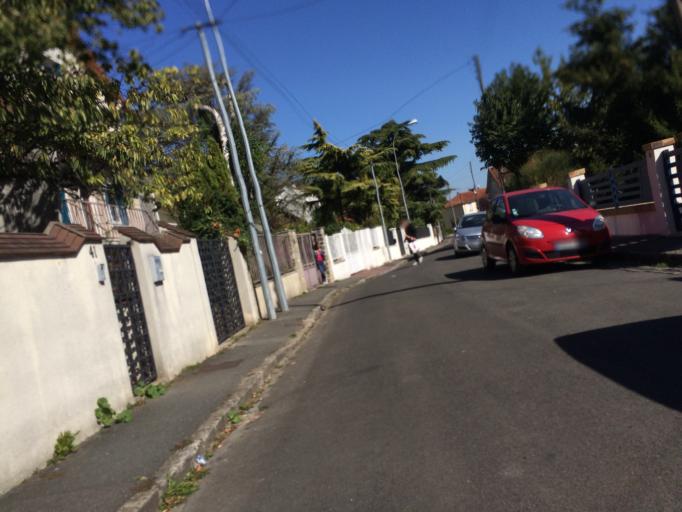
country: FR
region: Ile-de-France
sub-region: Departement de l'Essonne
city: Juvisy-sur-Orge
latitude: 48.6872
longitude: 2.3687
